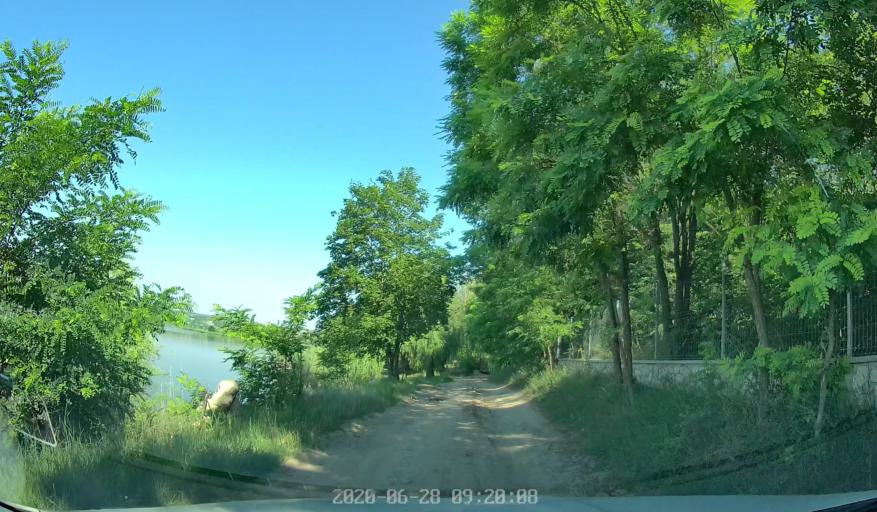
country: MD
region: Laloveni
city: Ialoveni
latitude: 46.9823
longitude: 28.7047
